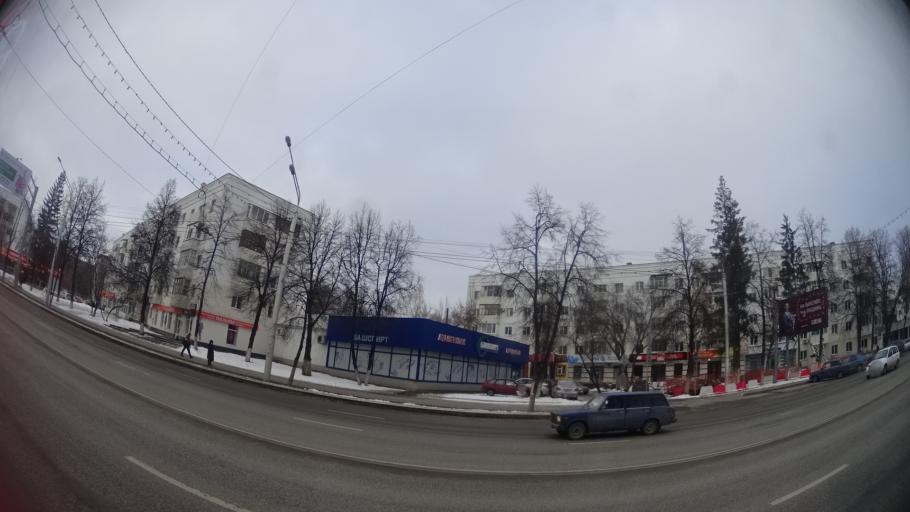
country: RU
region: Bashkortostan
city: Ufa
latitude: 54.7357
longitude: 55.9641
